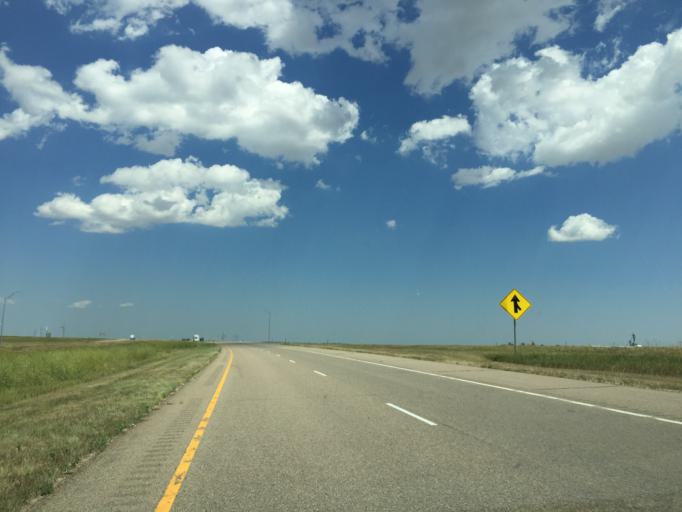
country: US
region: Colorado
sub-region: Lincoln County
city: Hugo
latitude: 39.2749
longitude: -103.4883
